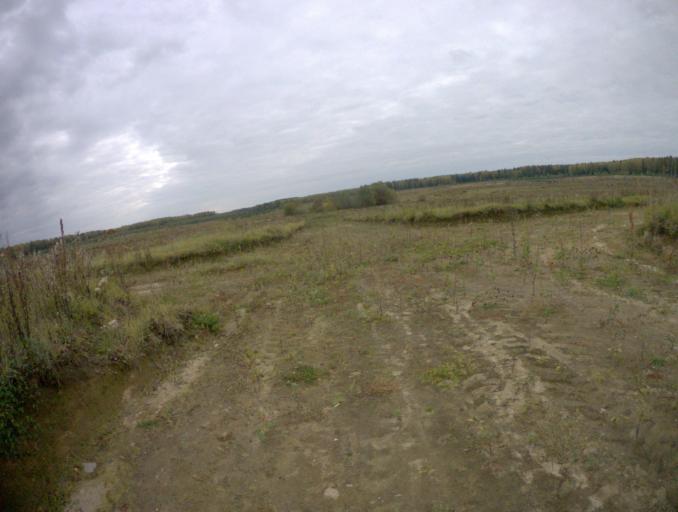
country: RU
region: Vladimir
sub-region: Kovrovskiy Rayon
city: Kovrov
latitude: 56.3512
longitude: 41.4453
